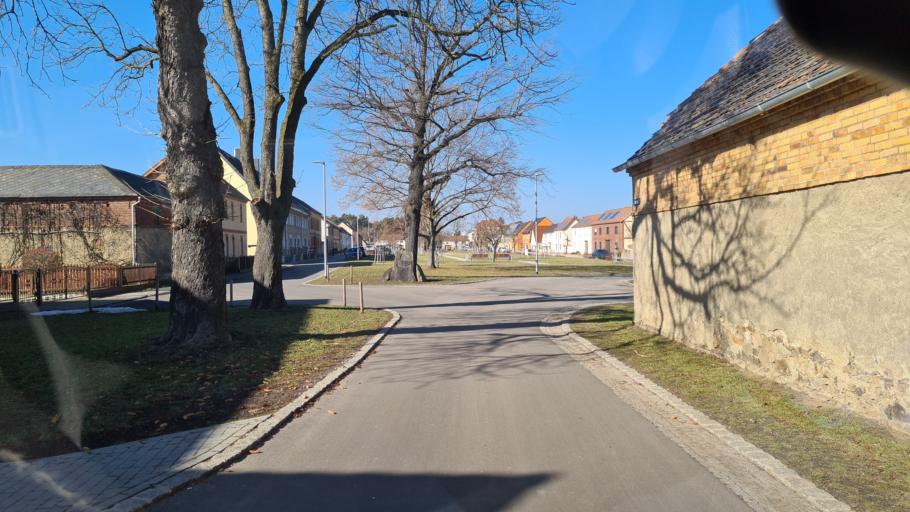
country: DE
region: Brandenburg
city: Senftenberg
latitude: 51.4948
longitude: 14.0636
